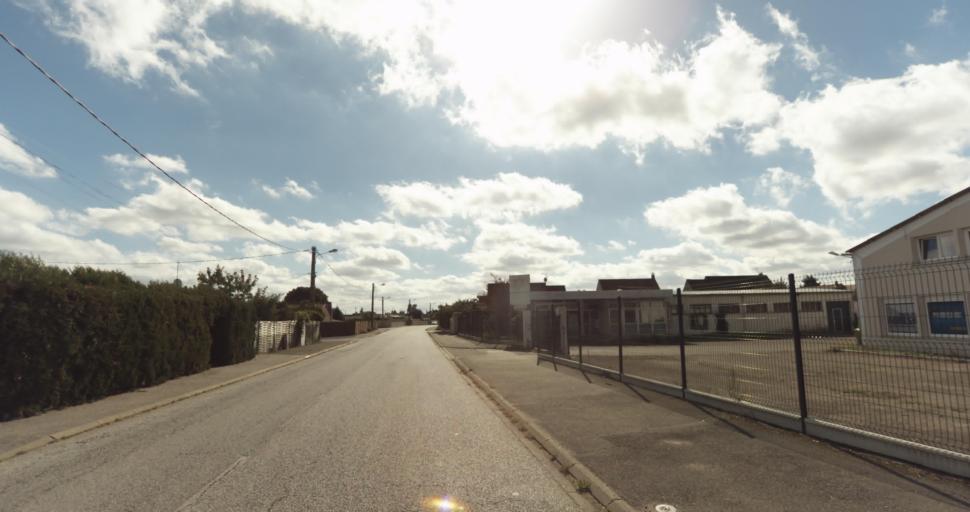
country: FR
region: Centre
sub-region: Departement d'Eure-et-Loir
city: Garnay
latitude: 48.7314
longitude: 1.3261
